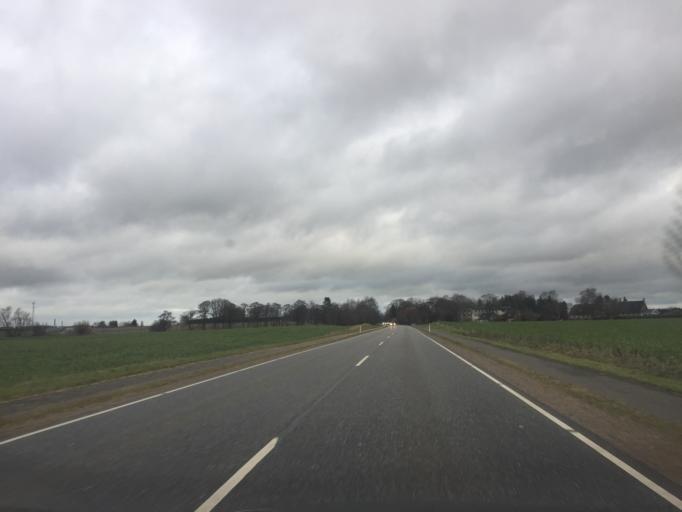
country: DK
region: Zealand
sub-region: Soro Kommune
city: Stenlille
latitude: 55.5473
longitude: 11.6121
